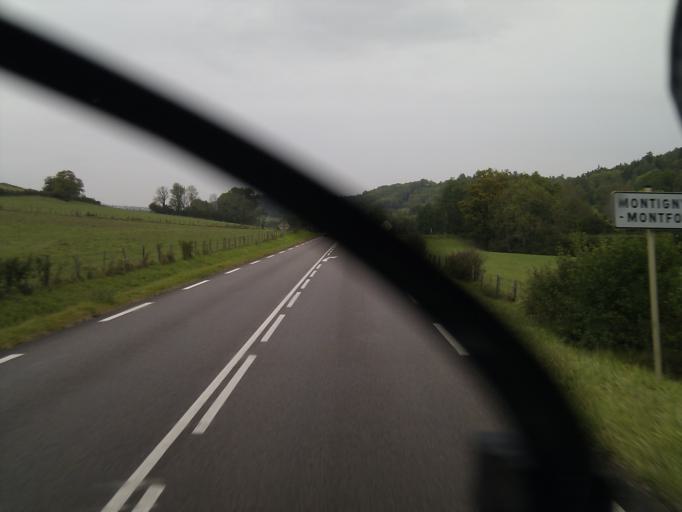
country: FR
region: Bourgogne
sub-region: Departement de la Cote-d'Or
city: Montbard
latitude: 47.5850
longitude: 4.3350
